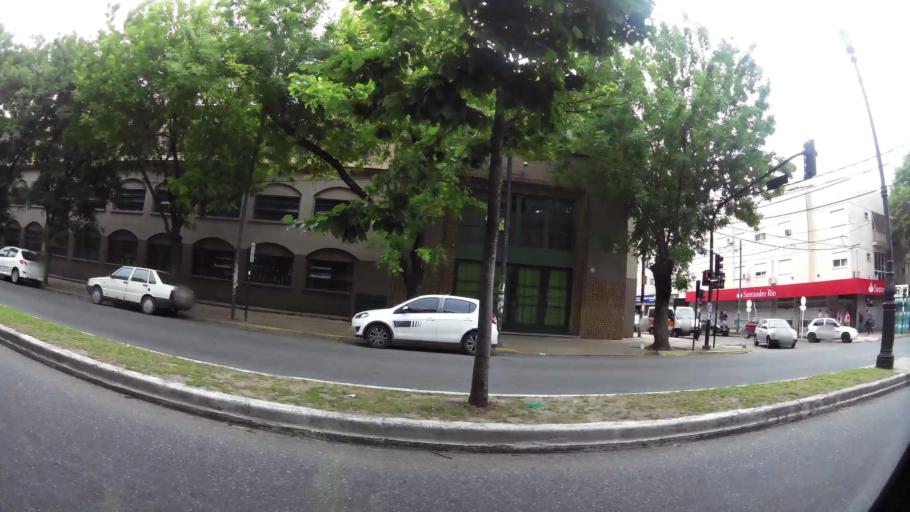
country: AR
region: Buenos Aires
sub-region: Partido de La Plata
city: La Plata
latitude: -34.9314
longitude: -57.9780
